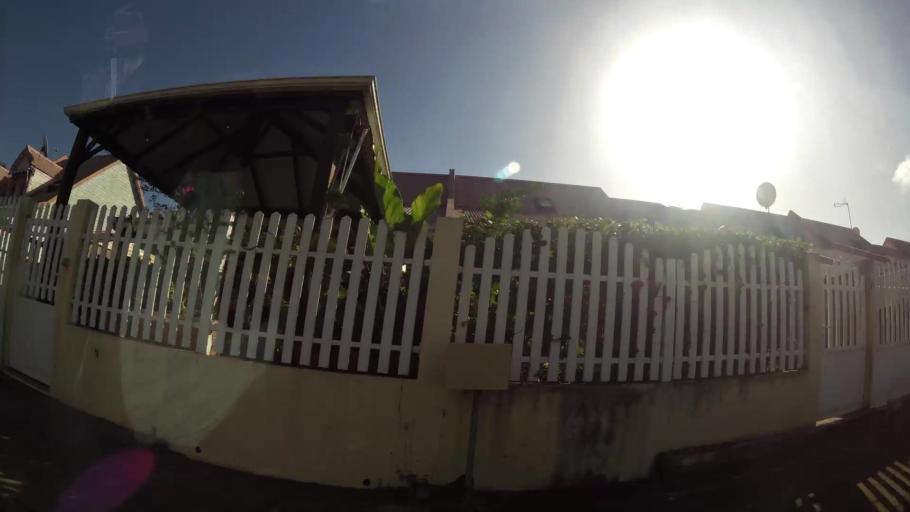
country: MQ
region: Martinique
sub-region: Martinique
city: Le Francois
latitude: 14.6224
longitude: -60.9017
